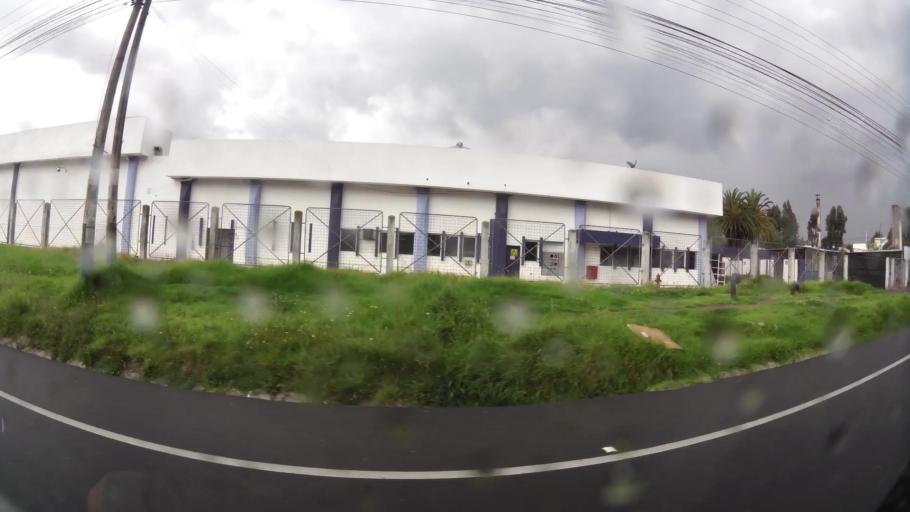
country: EC
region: Pichincha
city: Quito
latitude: -0.0974
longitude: -78.4895
